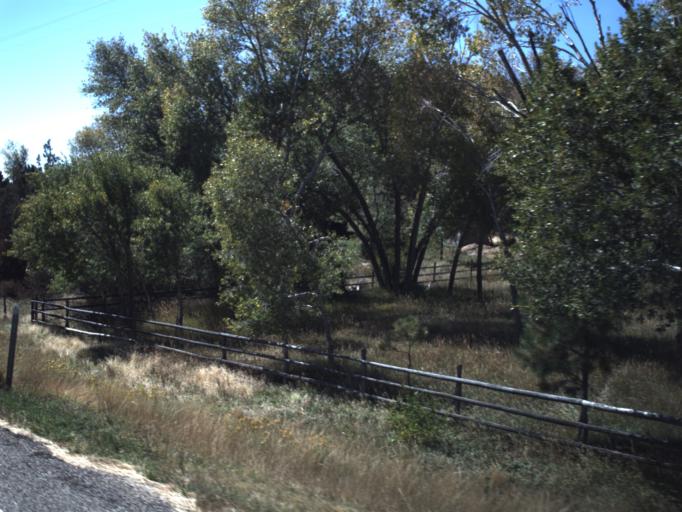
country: US
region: Utah
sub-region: Wayne County
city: Loa
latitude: 37.9130
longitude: -111.4243
